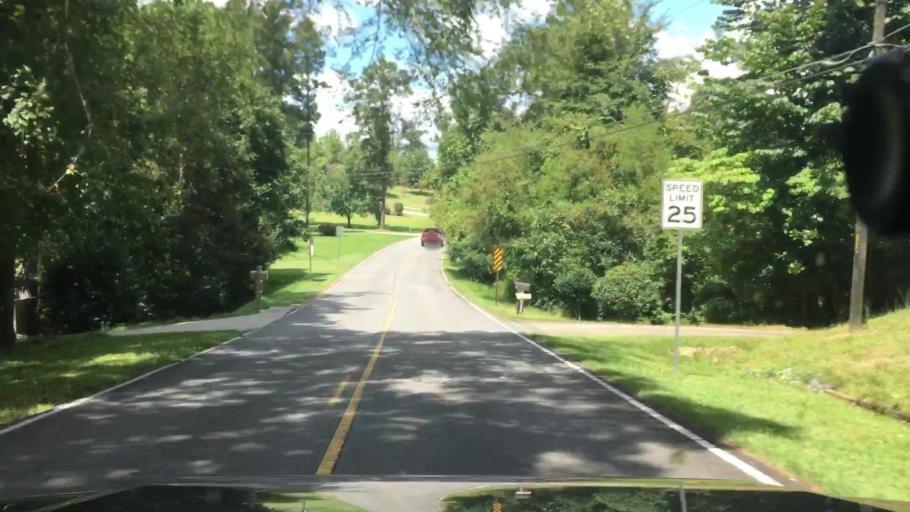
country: US
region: Georgia
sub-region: Bibb County
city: West Point
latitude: 32.8115
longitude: -83.7914
